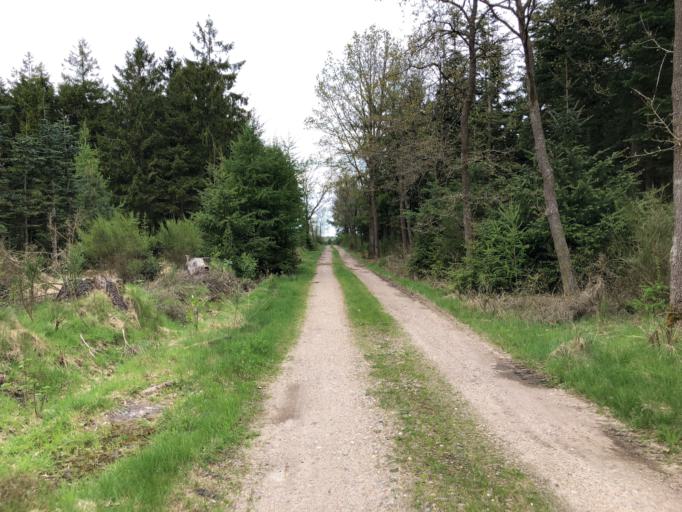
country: DK
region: Central Jutland
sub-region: Holstebro Kommune
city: Ulfborg
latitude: 56.2932
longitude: 8.4262
